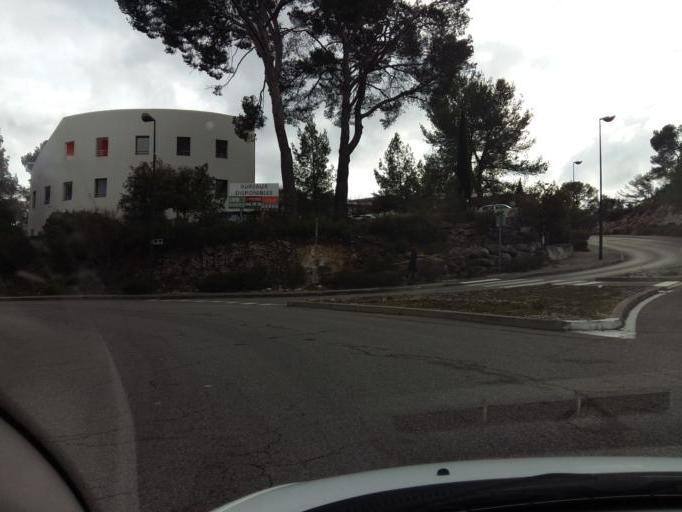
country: FR
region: Provence-Alpes-Cote d'Azur
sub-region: Departement des Bouches-du-Rhone
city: Cabries
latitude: 43.4899
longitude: 5.3564
